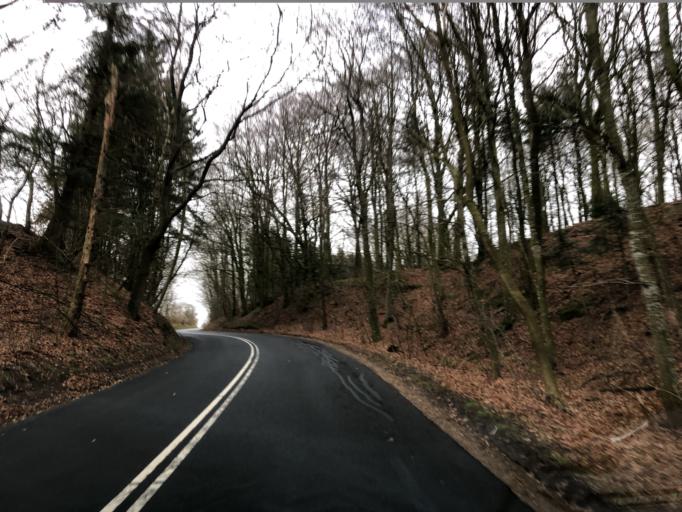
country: DK
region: Central Jutland
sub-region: Viborg Kommune
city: Stoholm
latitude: 56.4616
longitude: 9.1402
